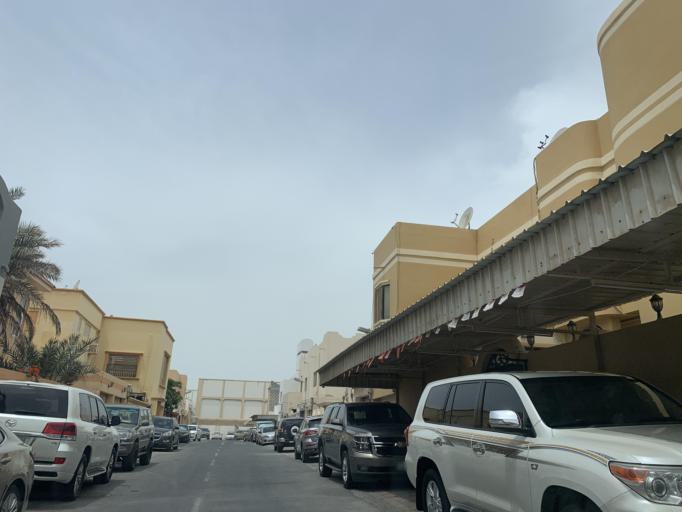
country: BH
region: Northern
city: Ar Rifa'
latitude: 26.1342
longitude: 50.5651
